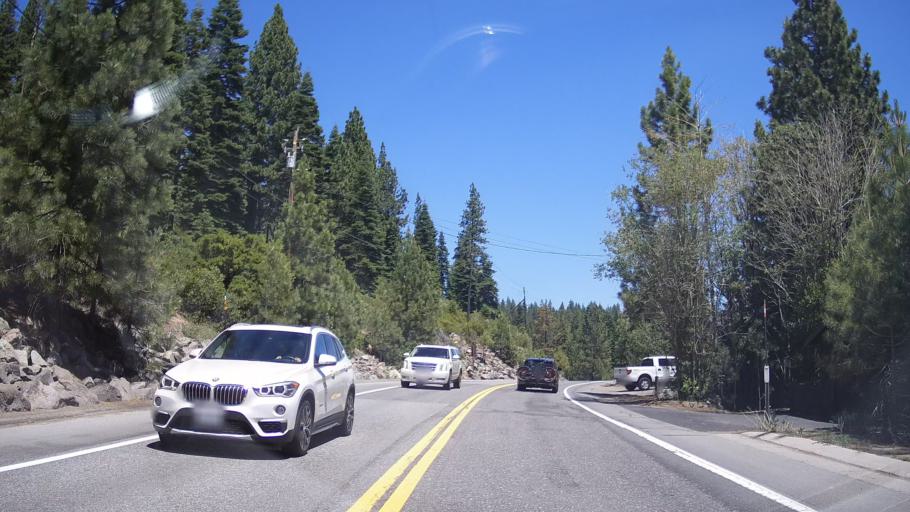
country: US
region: California
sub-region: Placer County
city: Dollar Point
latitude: 39.2031
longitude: -120.0960
